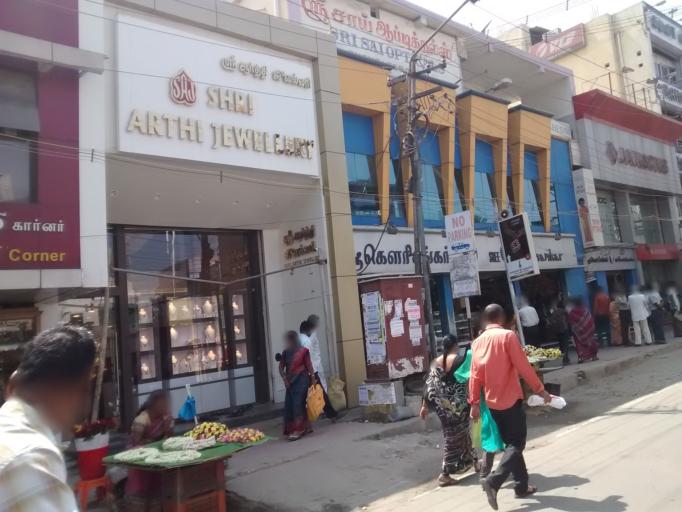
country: IN
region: Tamil Nadu
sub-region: Coimbatore
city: Coimbatore
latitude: 11.0170
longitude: 76.9681
